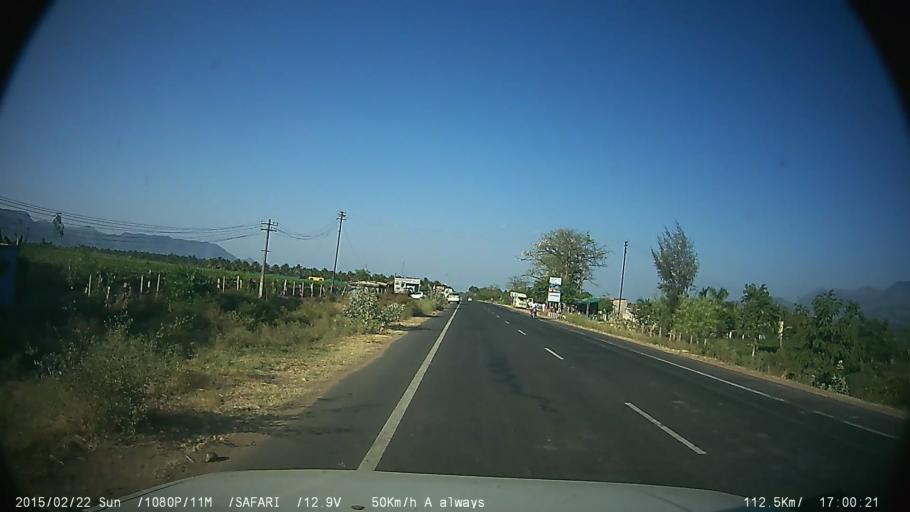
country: IN
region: Tamil Nadu
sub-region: Theni
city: Gudalur
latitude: 9.7007
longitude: 77.2602
